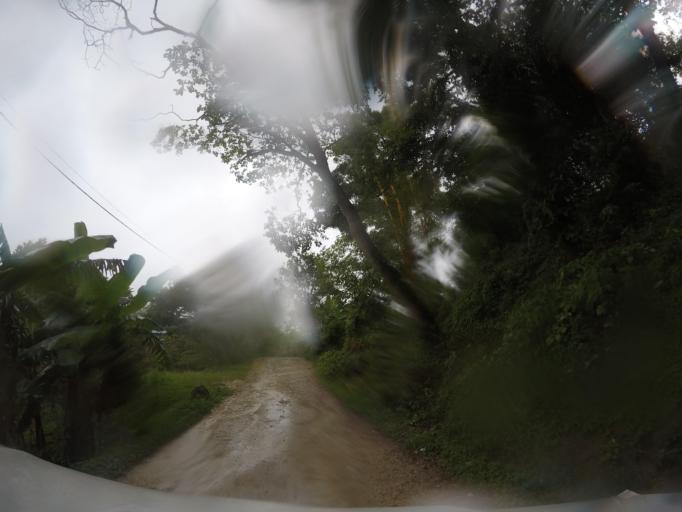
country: TL
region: Baucau
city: Venilale
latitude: -8.6408
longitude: 126.3842
